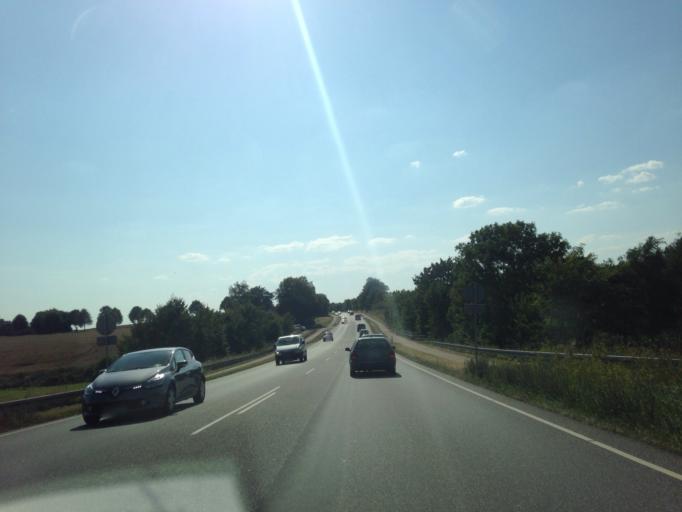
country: DK
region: Zealand
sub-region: Ringsted Kommune
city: Ringsted
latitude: 55.4788
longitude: 11.8382
